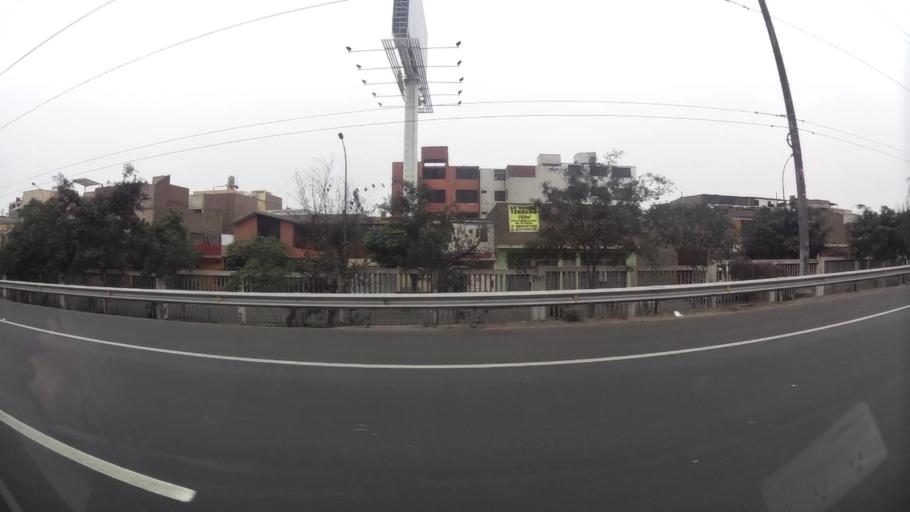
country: PE
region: Lima
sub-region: Lima
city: Surco
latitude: -12.1391
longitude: -76.9809
